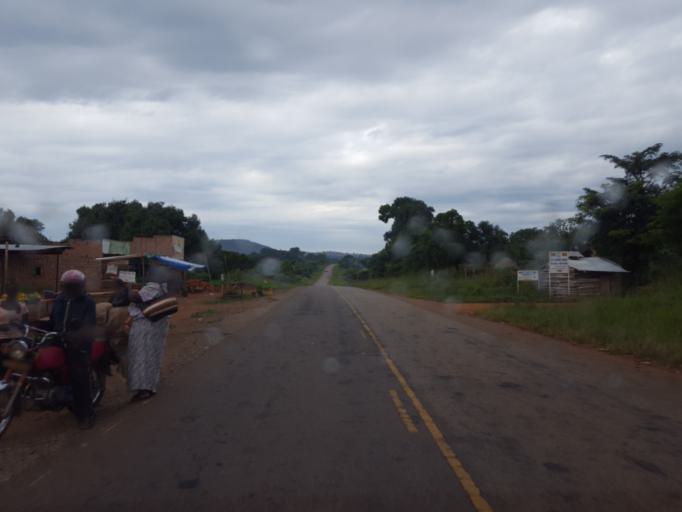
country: UG
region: Central Region
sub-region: Kiboga District
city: Kiboga
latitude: 0.9992
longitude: 31.7002
